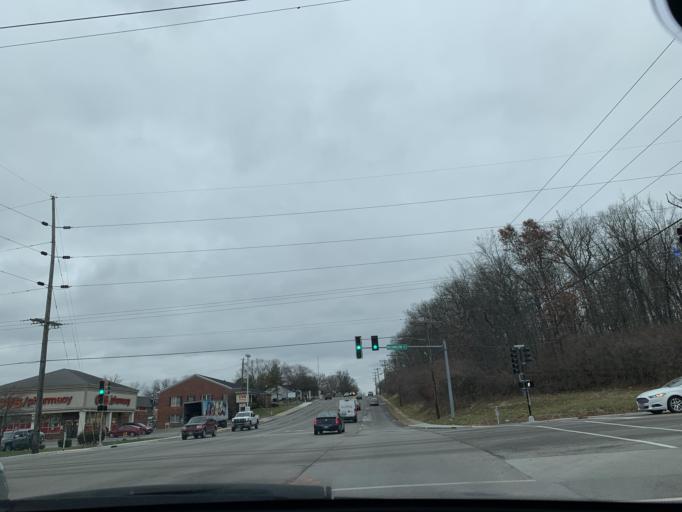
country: US
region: Illinois
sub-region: Sangamon County
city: Leland Grove
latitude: 39.8012
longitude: -89.6869
